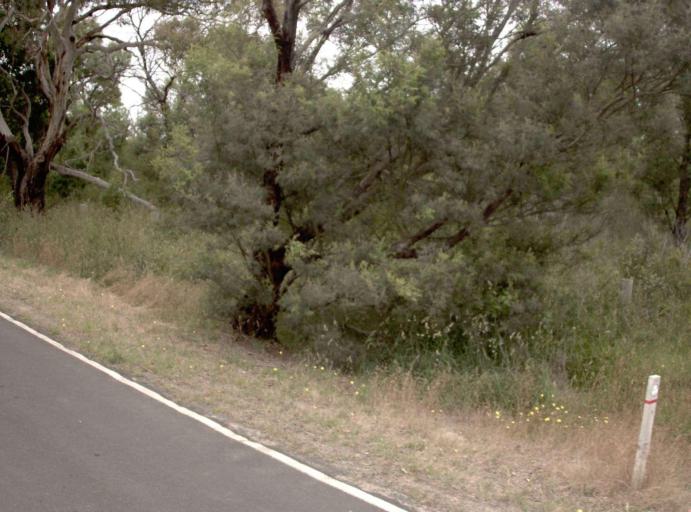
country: AU
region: Victoria
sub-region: Latrobe
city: Traralgon
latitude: -38.4864
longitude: 146.8201
